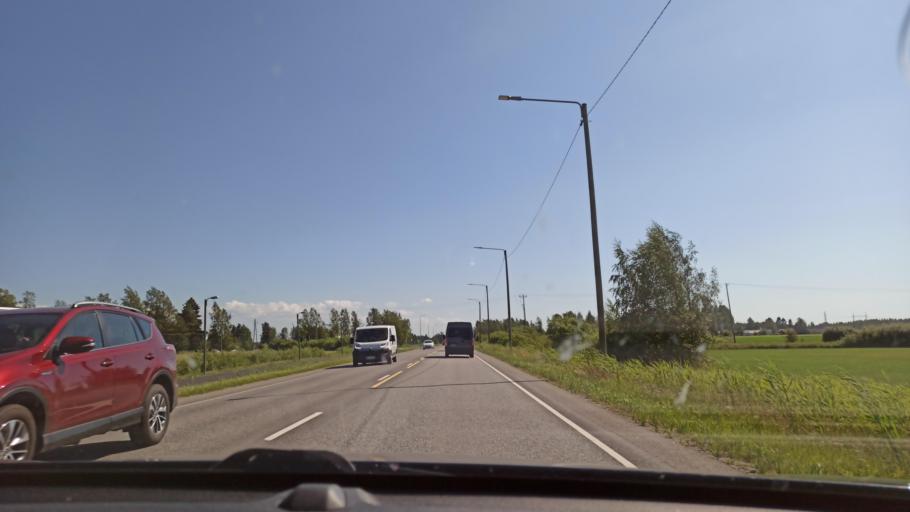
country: FI
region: Satakunta
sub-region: Pori
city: Pori
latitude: 61.5206
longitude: 21.8027
